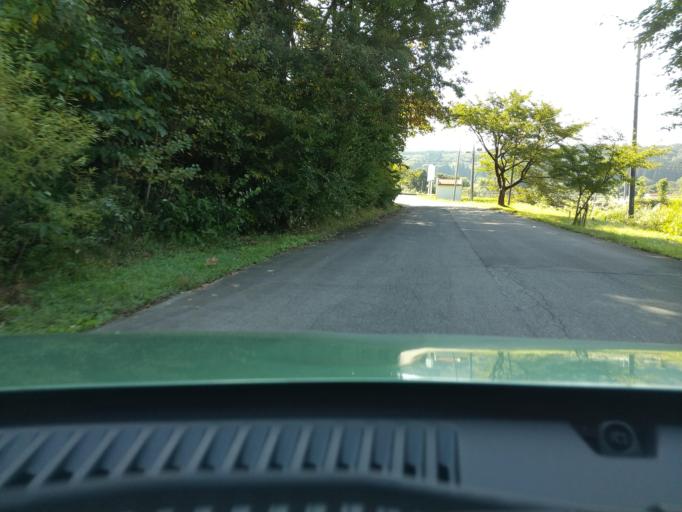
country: JP
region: Akita
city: Akita
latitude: 39.5958
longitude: 140.3012
